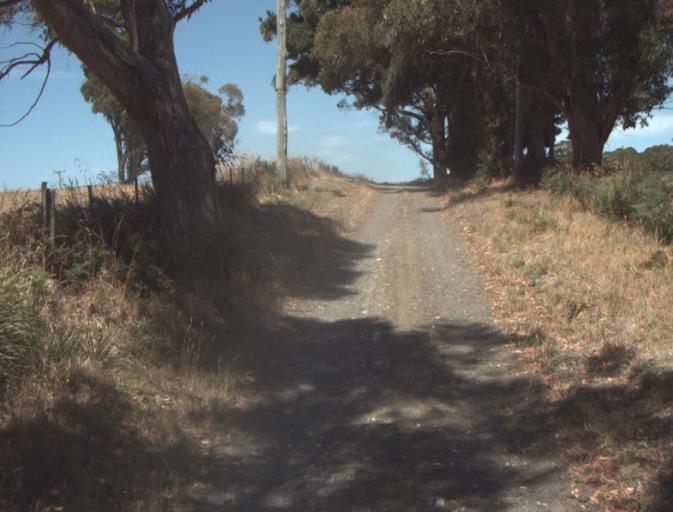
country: AU
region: Tasmania
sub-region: Launceston
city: Mayfield
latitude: -41.2410
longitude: 147.1280
